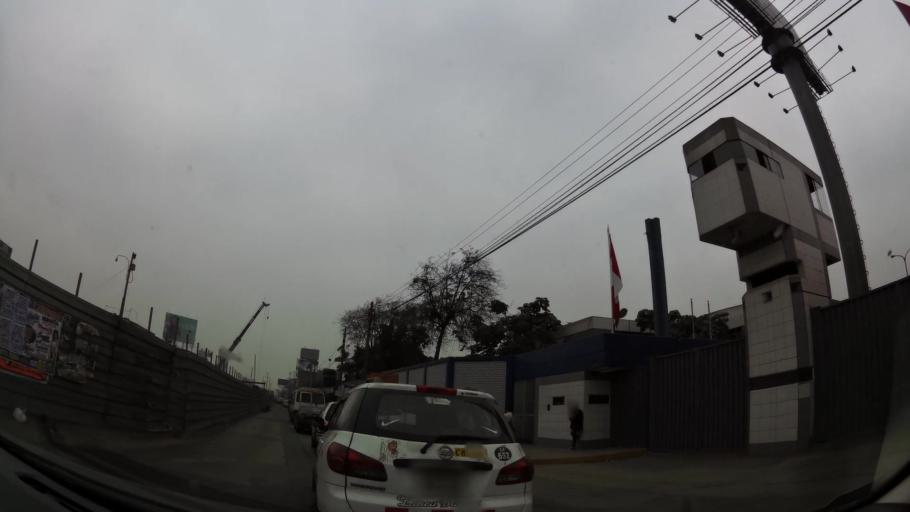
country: PE
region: Lima
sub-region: Lima
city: La Molina
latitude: -12.0525
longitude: -76.9599
